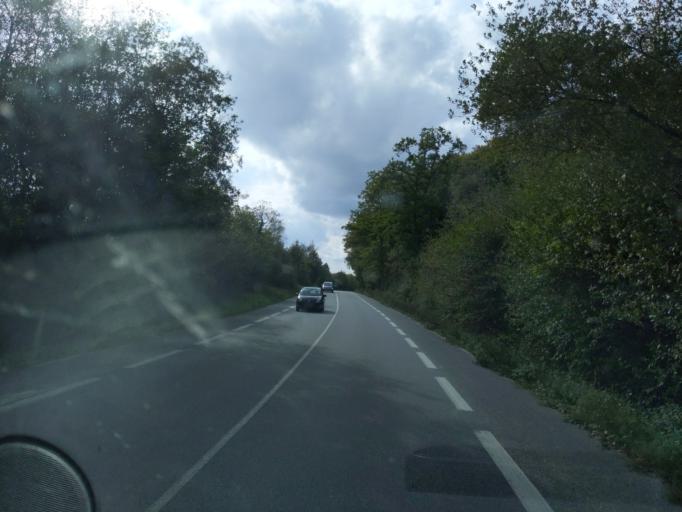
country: FR
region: Ile-de-France
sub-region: Departement des Yvelines
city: Rambouillet
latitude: 48.6527
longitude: 1.8766
